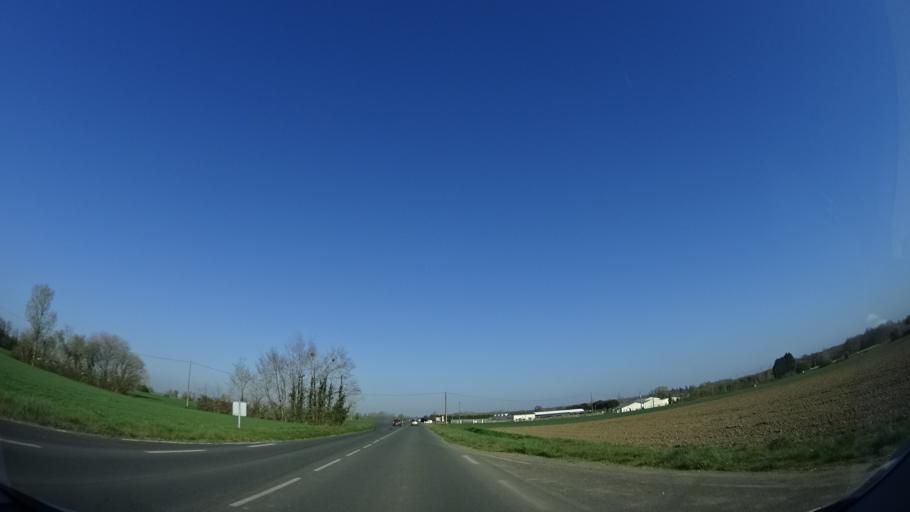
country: FR
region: Pays de la Loire
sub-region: Departement de Maine-et-Loire
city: Doue-la-Fontaine
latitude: 47.2067
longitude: -0.2937
